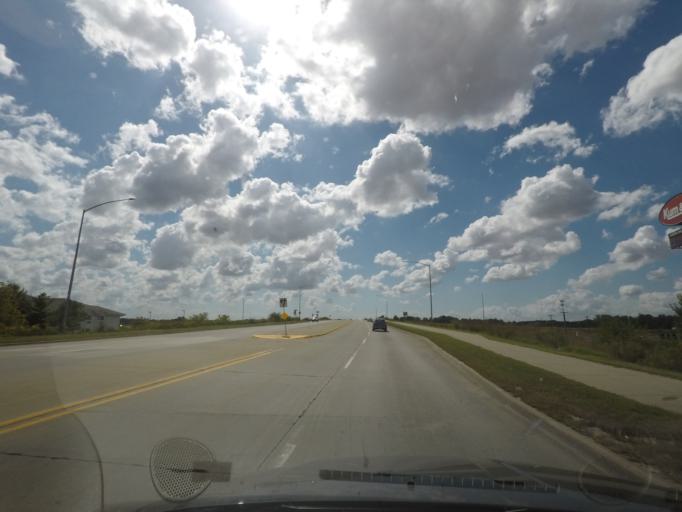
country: US
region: Iowa
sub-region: Story County
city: Ames
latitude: 42.0110
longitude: -93.6786
